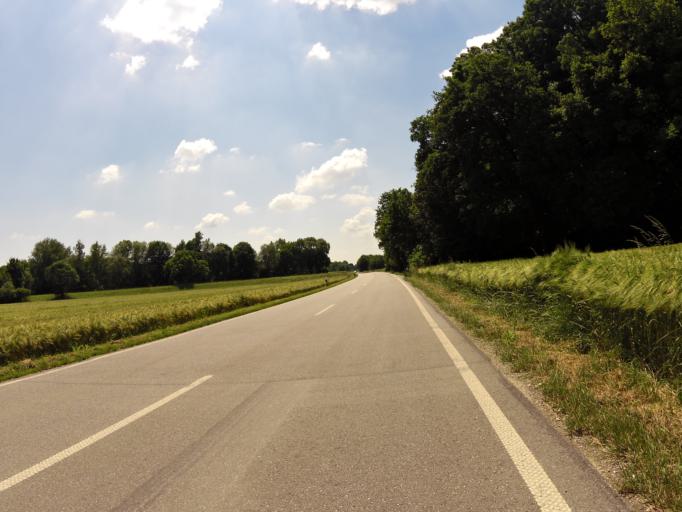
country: DE
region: Bavaria
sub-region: Upper Bavaria
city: Wang
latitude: 48.5120
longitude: 11.9773
